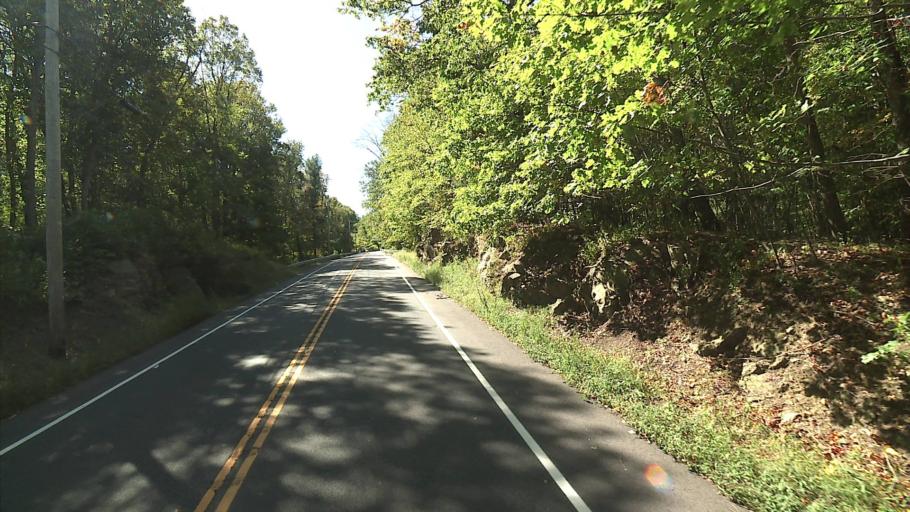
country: US
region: Connecticut
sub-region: New Haven County
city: Prospect
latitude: 41.4558
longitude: -72.9678
